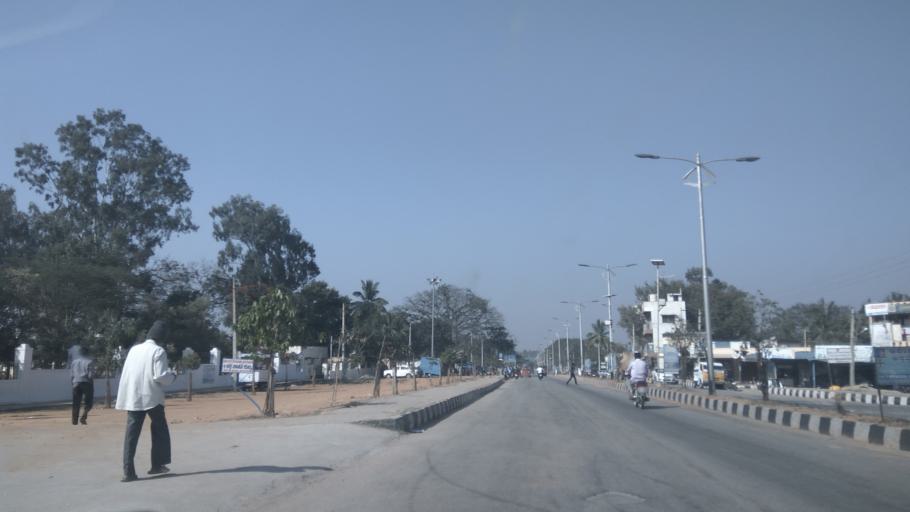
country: IN
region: Karnataka
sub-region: Bangalore Rural
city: Devanhalli
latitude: 13.2437
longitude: 77.7095
